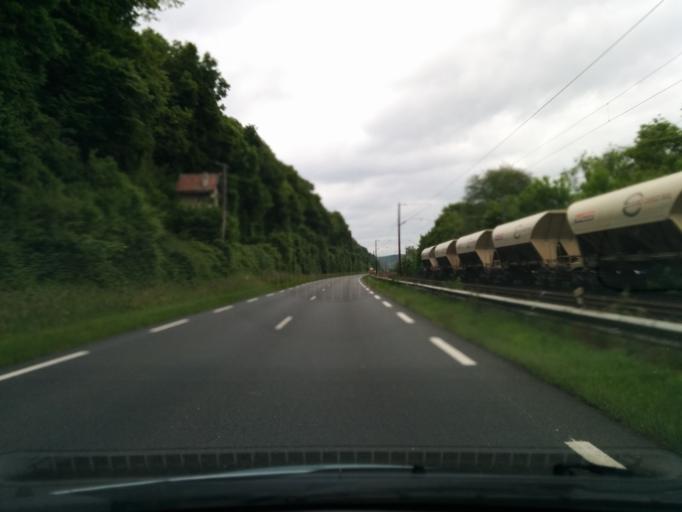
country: FR
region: Ile-de-France
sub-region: Departement des Yvelines
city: Bennecourt
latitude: 49.0491
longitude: 1.5293
